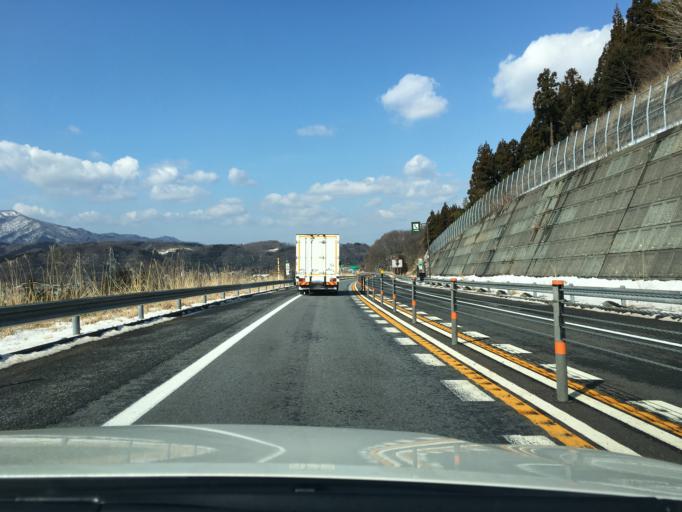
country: JP
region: Yamagata
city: Tsuruoka
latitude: 38.6052
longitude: 139.8430
